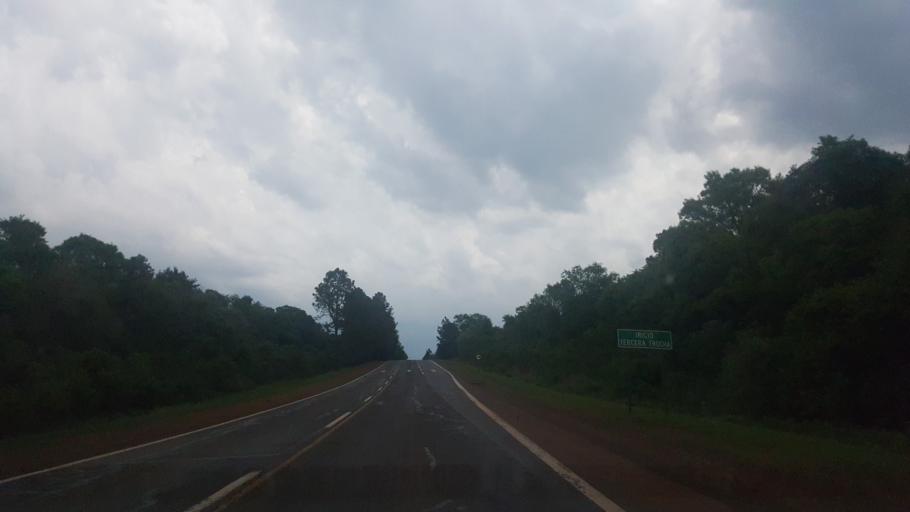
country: AR
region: Misiones
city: Santo Pipo
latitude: -27.1218
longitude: -55.3755
